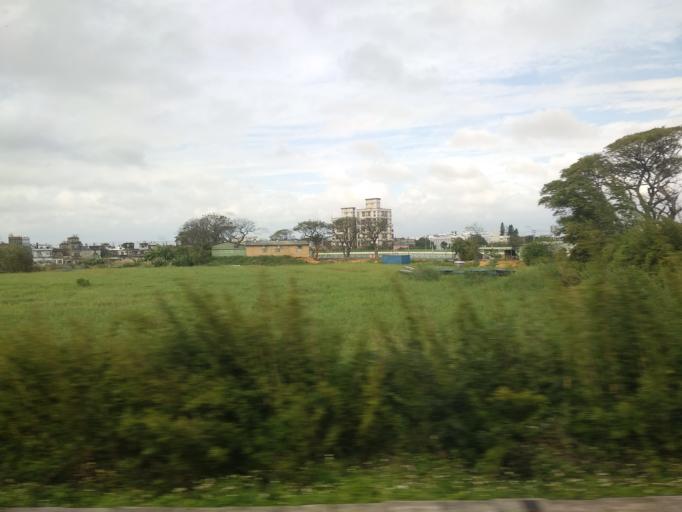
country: TW
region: Taiwan
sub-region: Hsinchu
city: Zhubei
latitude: 24.9098
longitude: 121.0478
